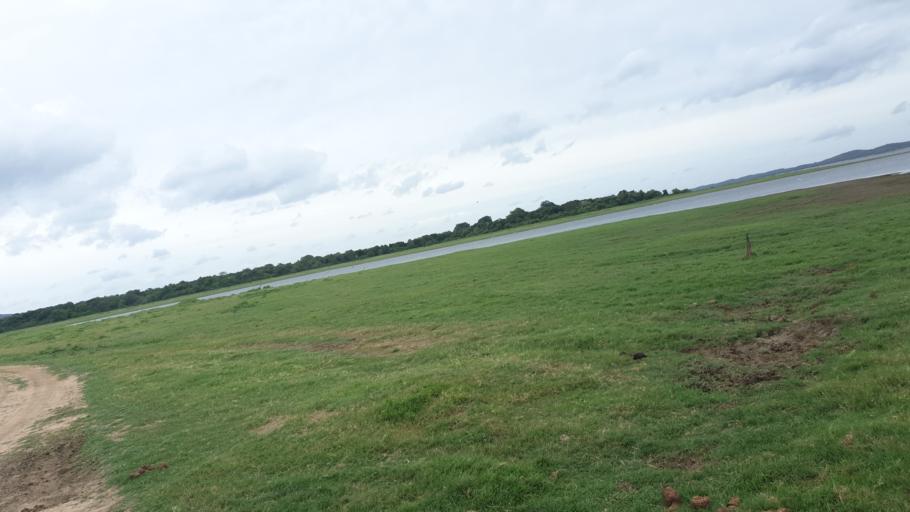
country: LK
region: North Central
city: Polonnaruwa
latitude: 8.1328
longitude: 80.9106
